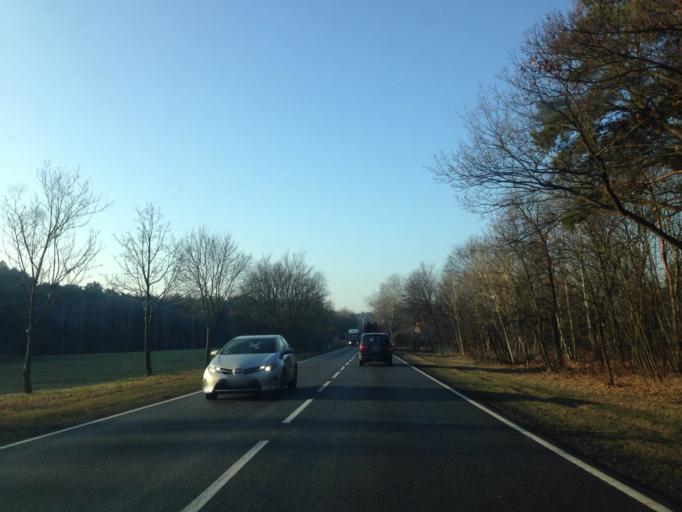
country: PL
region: Kujawsko-Pomorskie
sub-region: Powiat torunski
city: Zlawies Wielka
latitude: 53.0517
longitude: 18.3318
